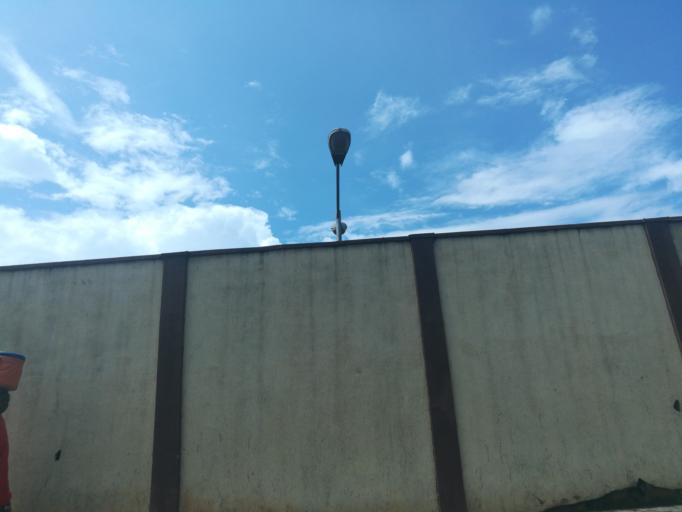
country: NG
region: Lagos
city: Agege
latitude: 6.6231
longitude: 3.3309
